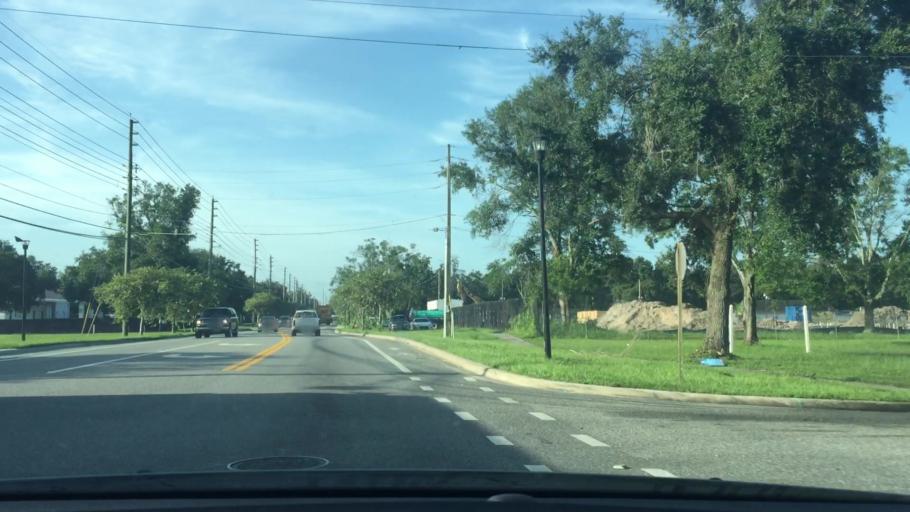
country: US
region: Florida
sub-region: Orange County
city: Pine Hills
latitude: 28.5670
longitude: -81.4306
